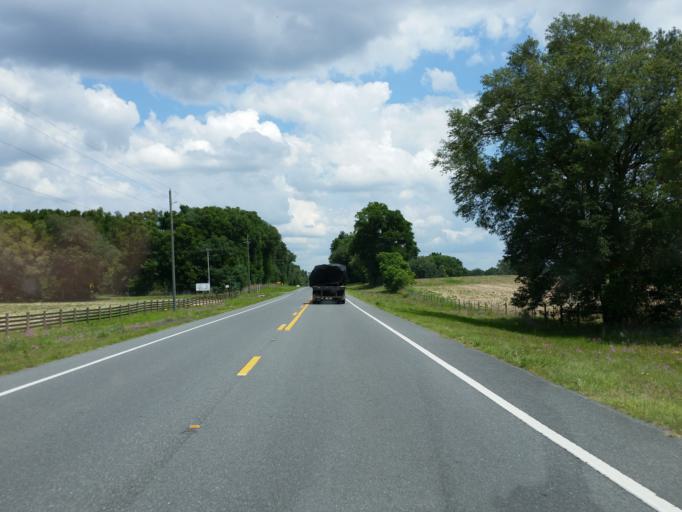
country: US
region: Florida
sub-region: Levy County
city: Williston Highlands
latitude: 29.2257
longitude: -82.4410
